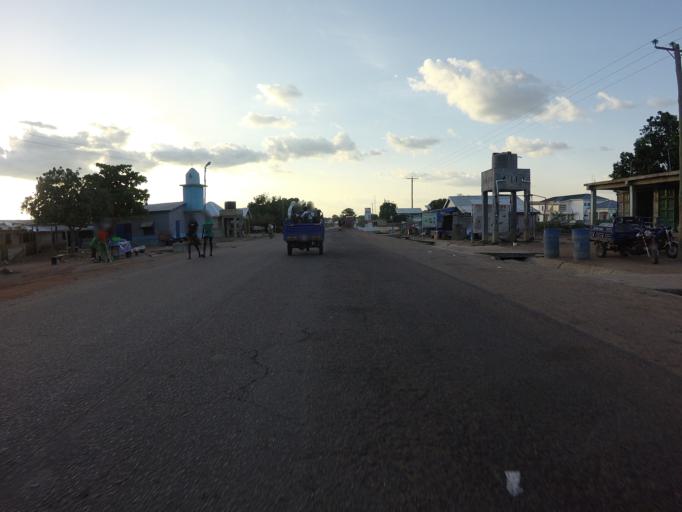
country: GH
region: Upper East
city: Navrongo
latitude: 10.9873
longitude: -1.1091
